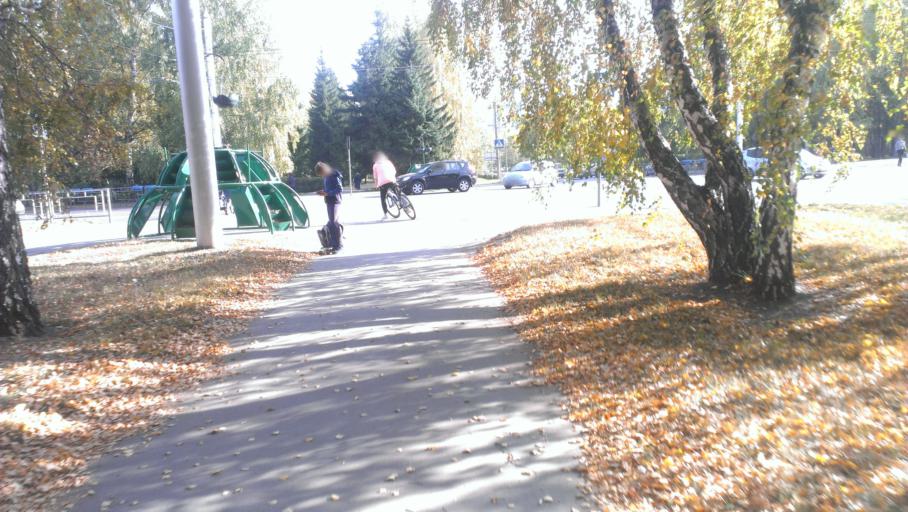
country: RU
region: Altai Krai
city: Novosilikatnyy
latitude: 53.3478
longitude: 83.6837
